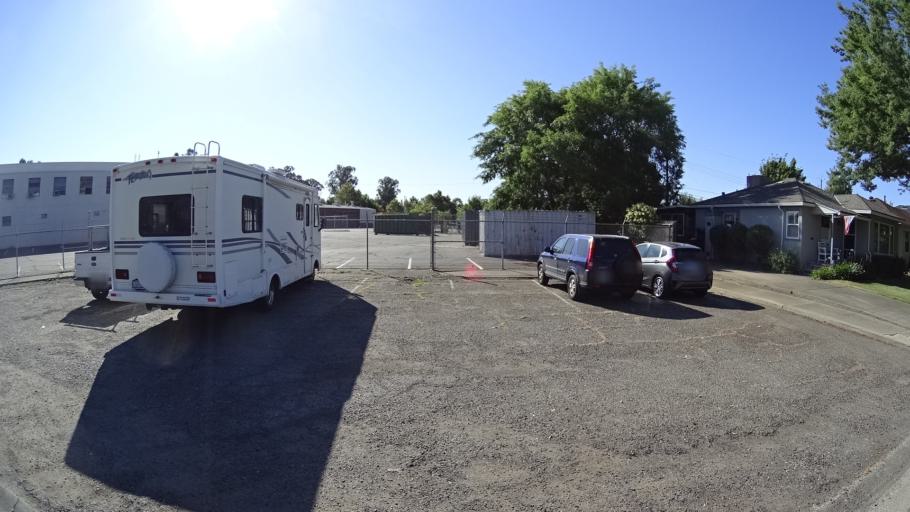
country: US
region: California
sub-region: Sacramento County
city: Sacramento
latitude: 38.5618
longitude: -121.4324
